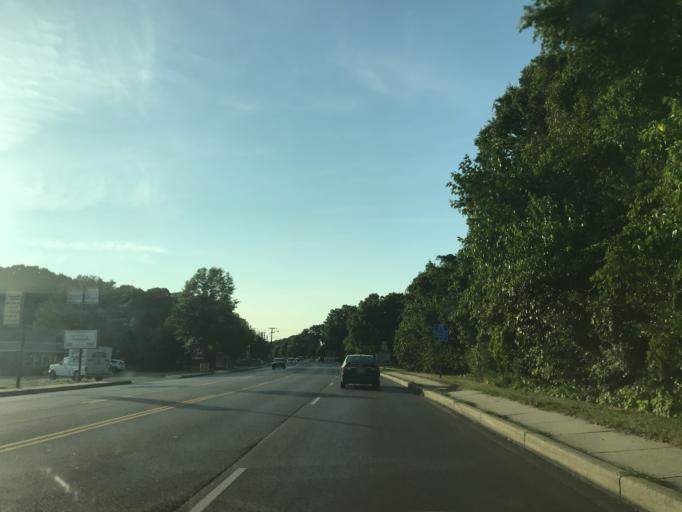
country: US
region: Maryland
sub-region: Anne Arundel County
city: Robinwood
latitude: 38.9622
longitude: -76.5113
